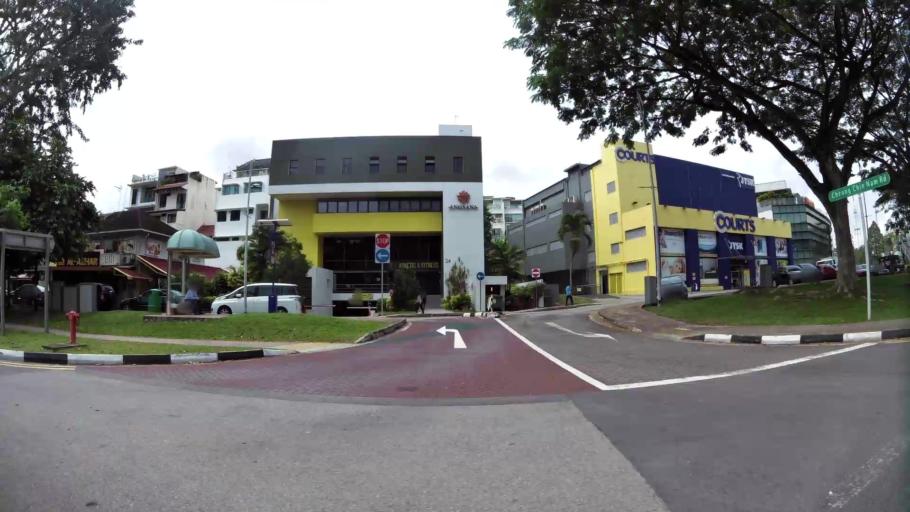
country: SG
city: Singapore
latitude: 1.3441
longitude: 103.7752
